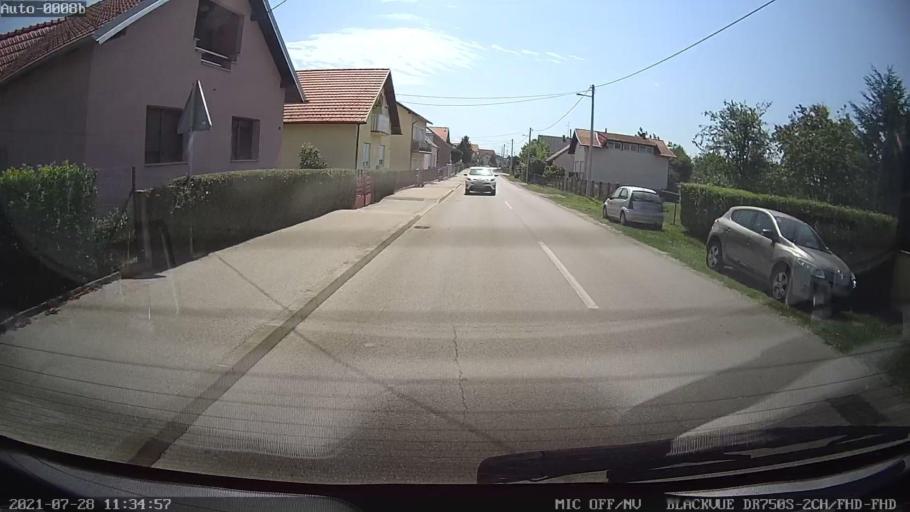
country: HR
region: Varazdinska
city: Varazdin
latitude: 46.2935
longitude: 16.3731
